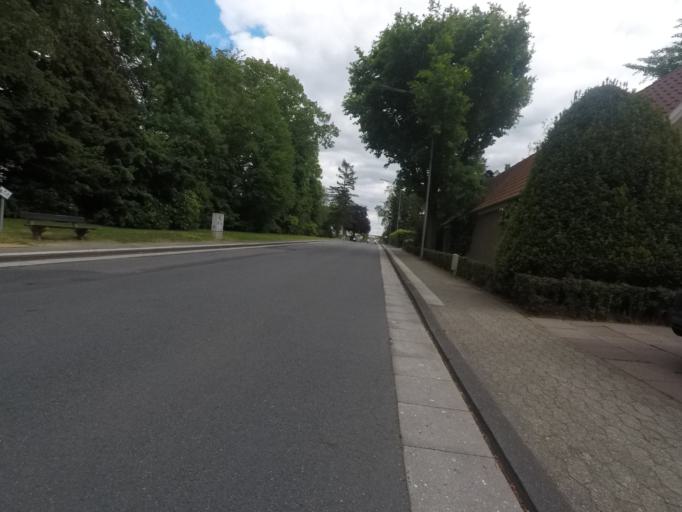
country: DE
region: North Rhine-Westphalia
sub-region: Regierungsbezirk Detmold
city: Herford
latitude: 52.1148
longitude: 8.6899
